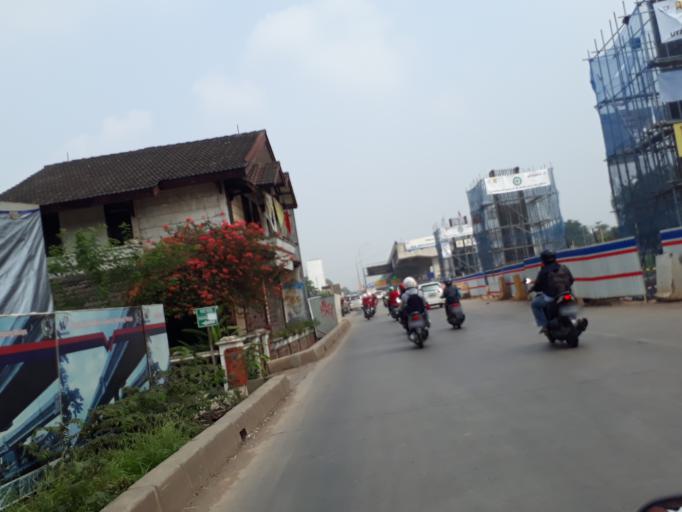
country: ID
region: West Java
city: Bekasi
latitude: -6.2497
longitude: 106.9660
